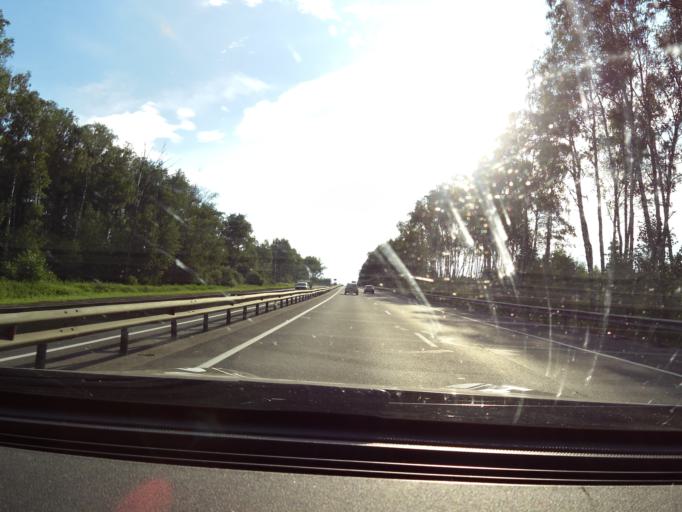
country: RU
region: Vladimir
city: Melekhovo
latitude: 56.2095
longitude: 41.2524
